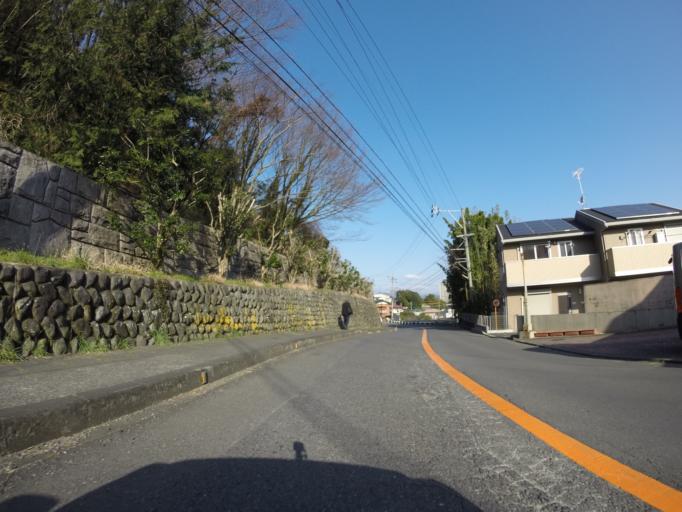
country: JP
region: Shizuoka
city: Shizuoka-shi
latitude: 34.9965
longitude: 138.4482
